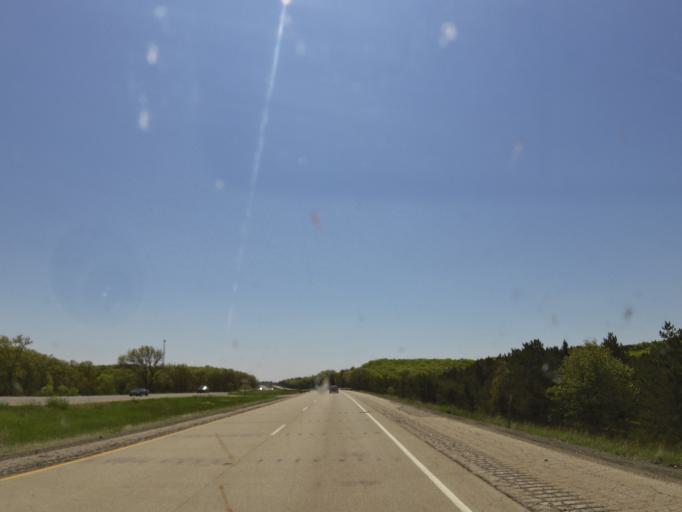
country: US
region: Wisconsin
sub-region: Monroe County
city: Tomah
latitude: 44.1467
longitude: -90.5481
